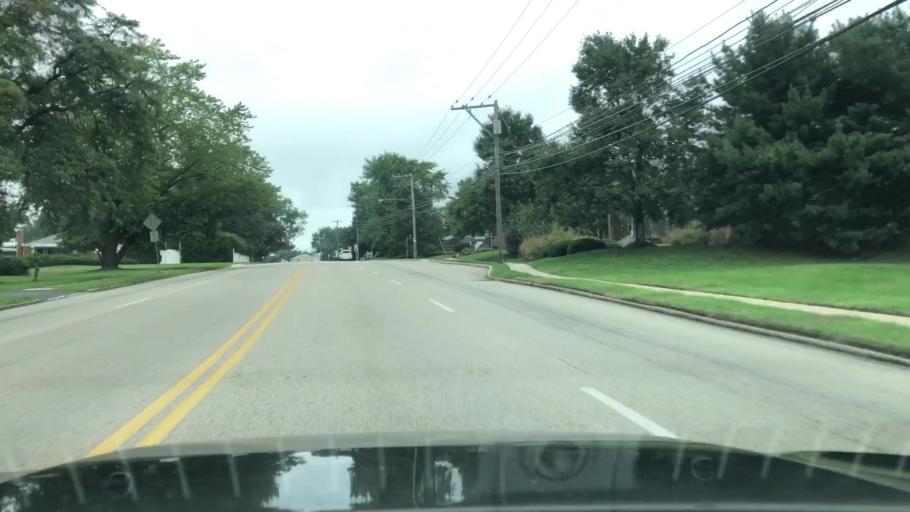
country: US
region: Pennsylvania
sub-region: Montgomery County
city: Norristown
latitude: 40.1337
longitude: -75.3018
